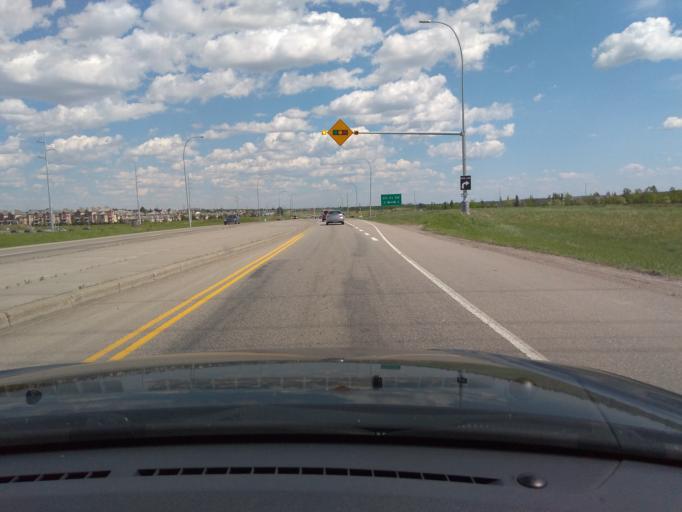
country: CA
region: Alberta
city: Calgary
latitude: 51.0156
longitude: -114.1993
